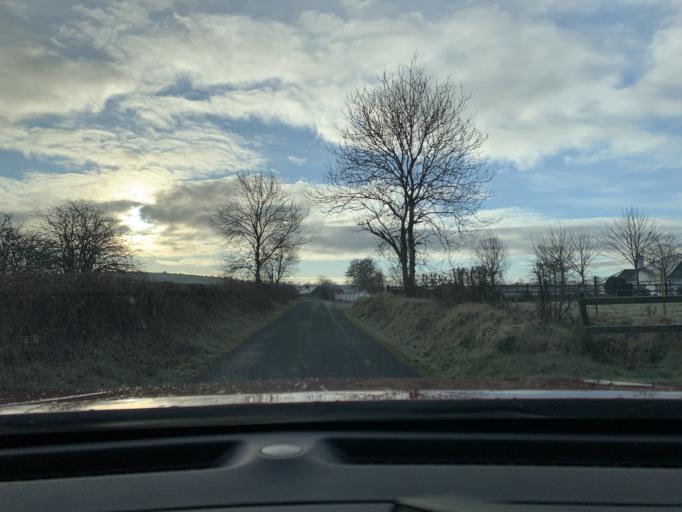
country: IE
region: Connaught
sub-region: Sligo
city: Ballymote
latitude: 54.1166
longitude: -8.5320
